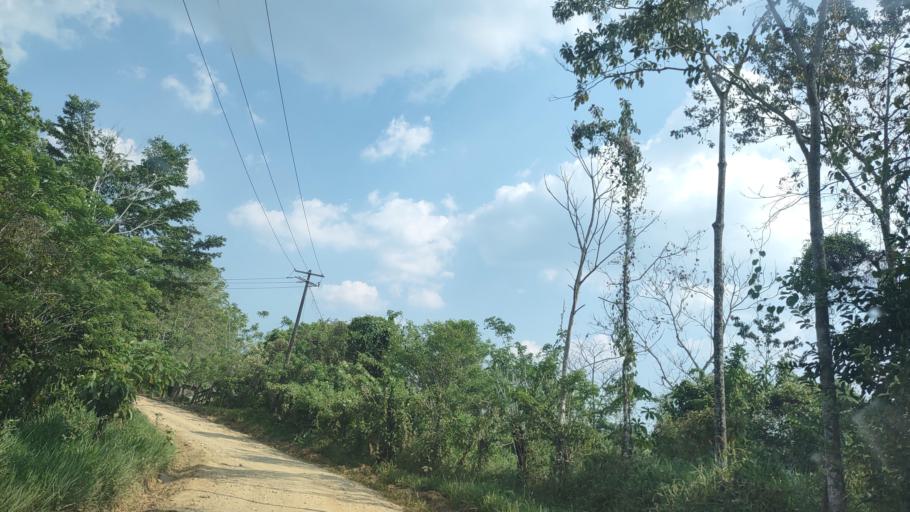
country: MX
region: Chiapas
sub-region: Tecpatan
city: Raudales Malpaso
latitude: 17.3276
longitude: -93.7468
